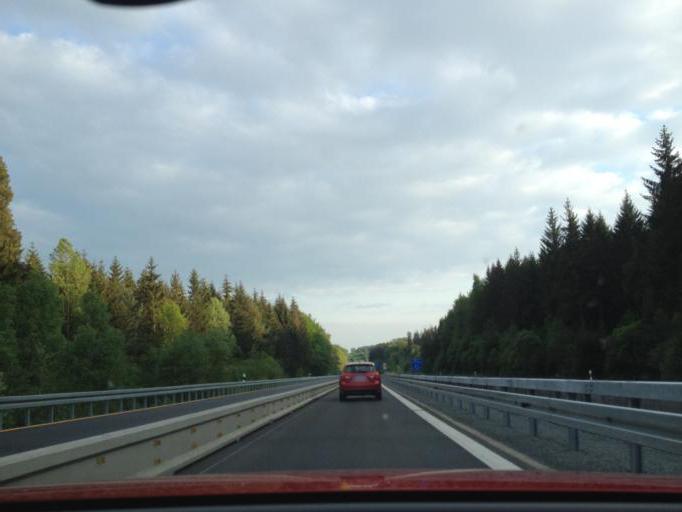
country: DE
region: Bavaria
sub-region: Upper Palatinate
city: Neustadt an der Waldnaab
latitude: 49.7517
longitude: 12.1541
